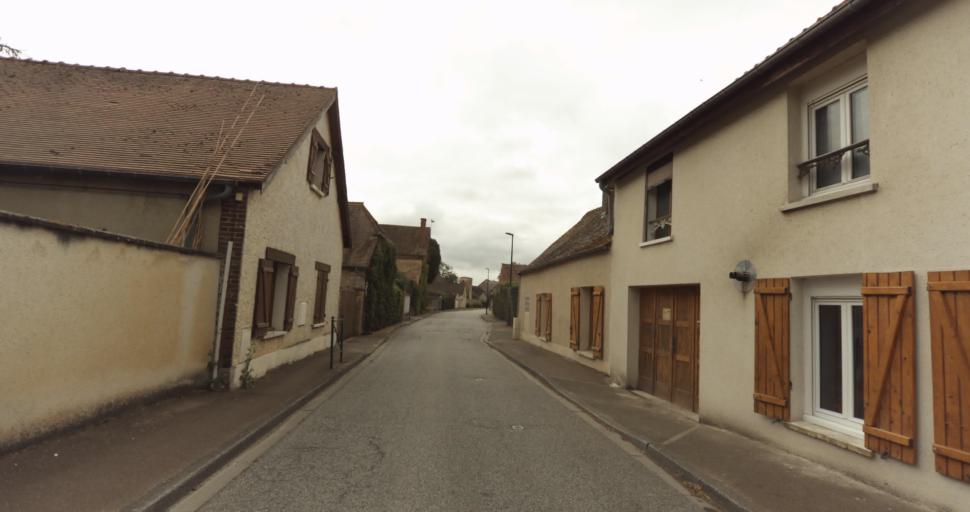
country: FR
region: Haute-Normandie
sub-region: Departement de l'Eure
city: Garennes-sur-Eure
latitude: 48.9125
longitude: 1.4370
